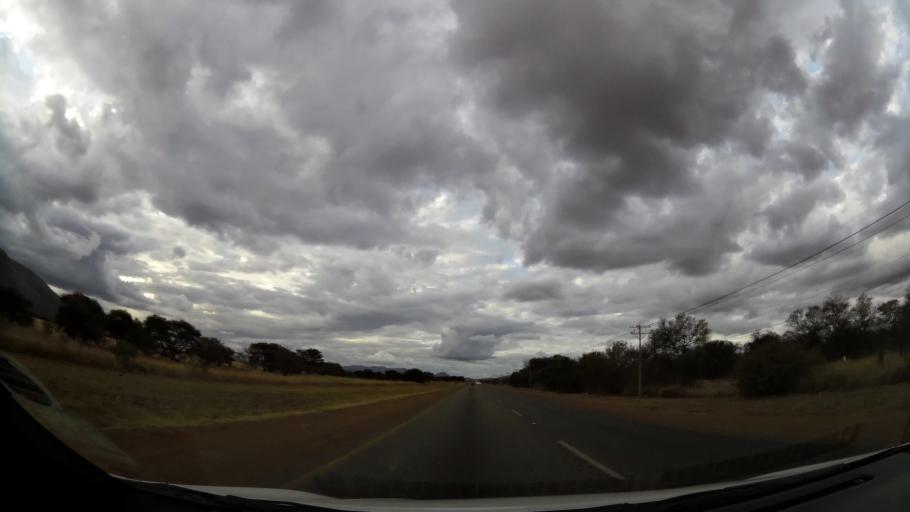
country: ZA
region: Limpopo
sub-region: Waterberg District Municipality
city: Mokopane
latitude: -24.2573
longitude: 28.9873
